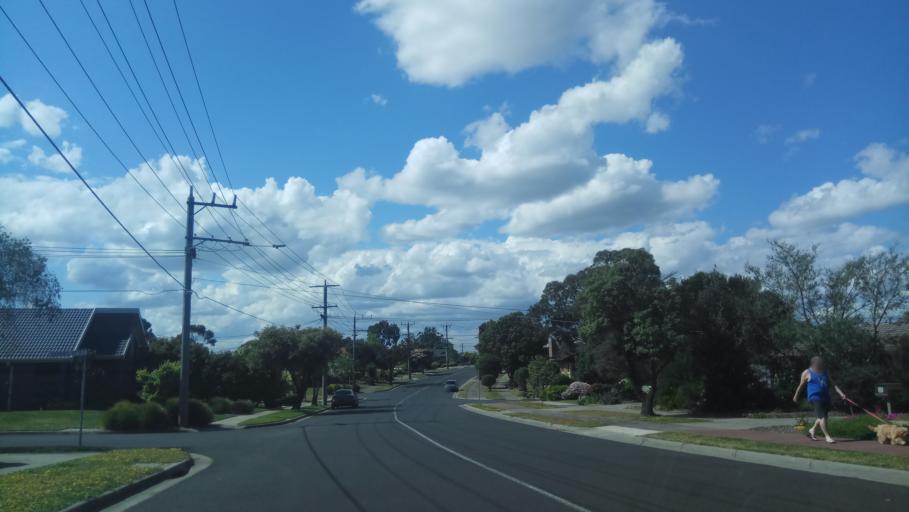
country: AU
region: Victoria
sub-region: Kingston
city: Dingley Village
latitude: -37.9755
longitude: 145.1175
